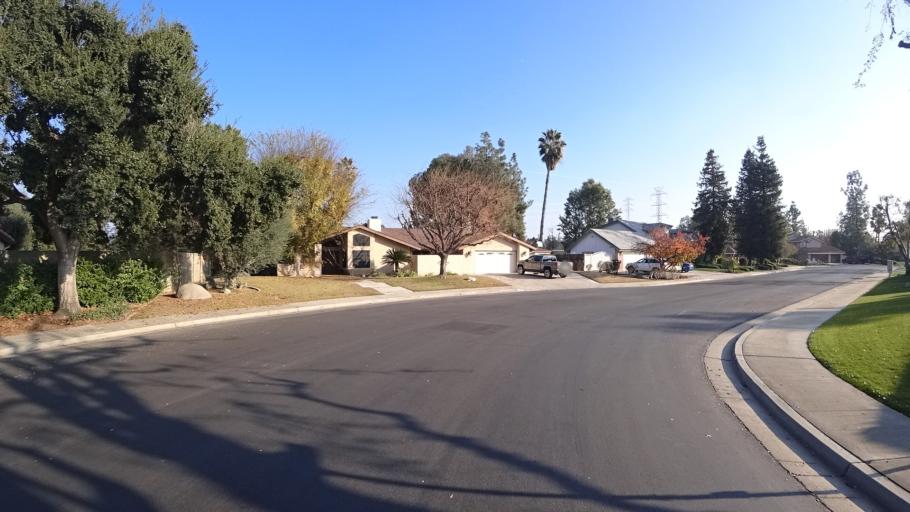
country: US
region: California
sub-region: Kern County
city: Greenacres
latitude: 35.3380
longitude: -119.0976
